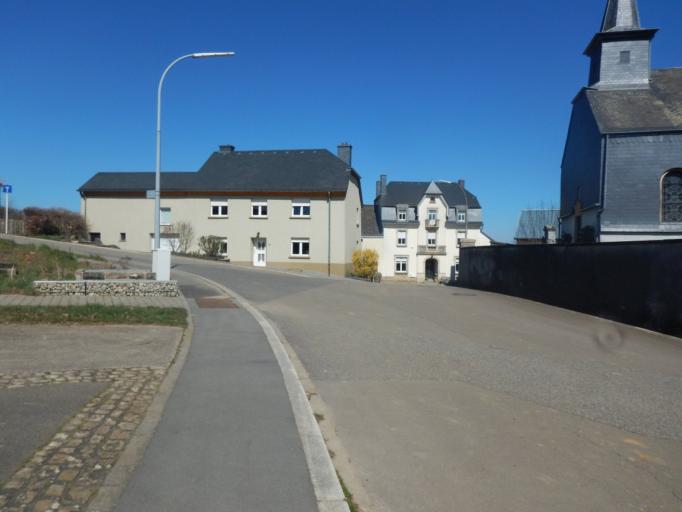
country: LU
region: Luxembourg
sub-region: Canton de Capellen
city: Garnich
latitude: 49.6014
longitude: 5.9467
